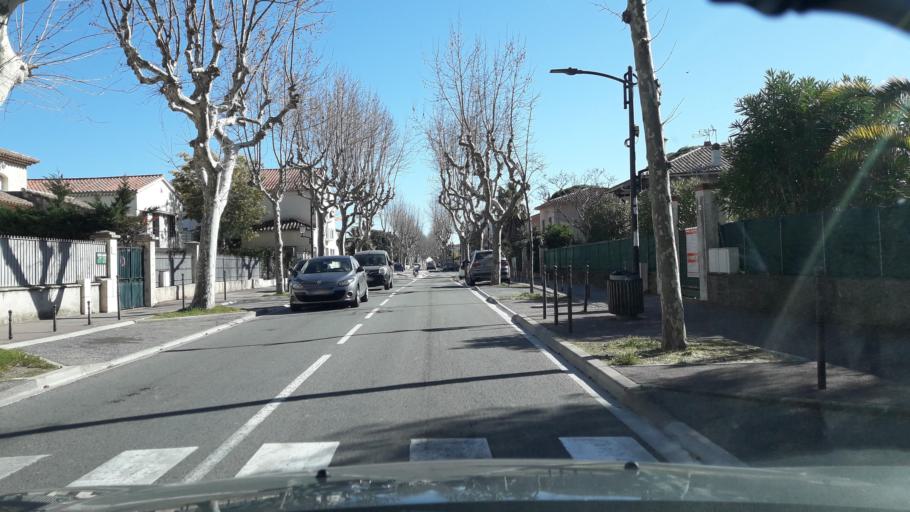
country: FR
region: Provence-Alpes-Cote d'Azur
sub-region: Departement du Var
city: Frejus
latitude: 43.4241
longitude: 6.7403
